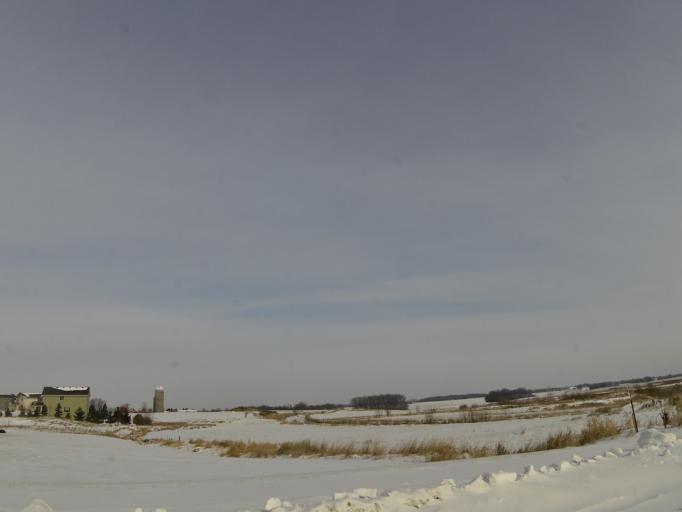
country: US
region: Minnesota
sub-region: Carver County
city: Mayer
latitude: 44.8918
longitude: -93.8735
